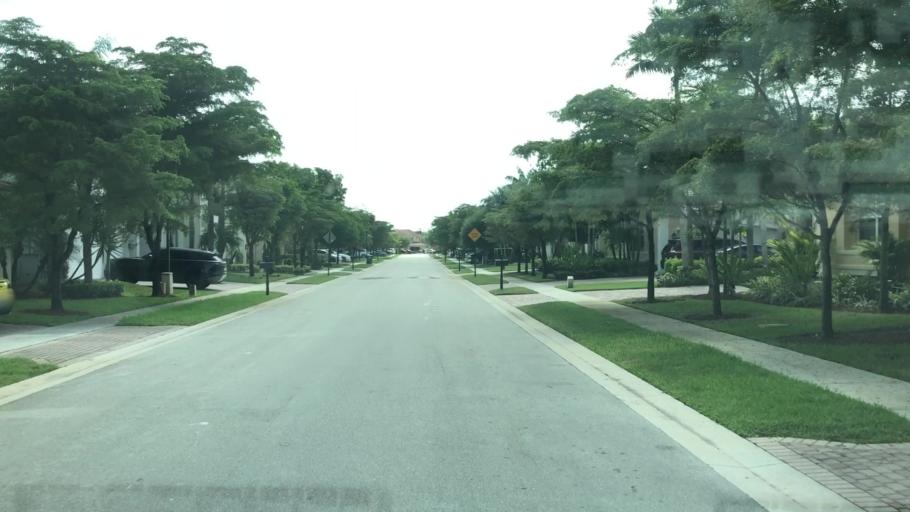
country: US
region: Florida
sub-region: Miami-Dade County
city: Palm Springs North
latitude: 25.9655
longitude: -80.3822
